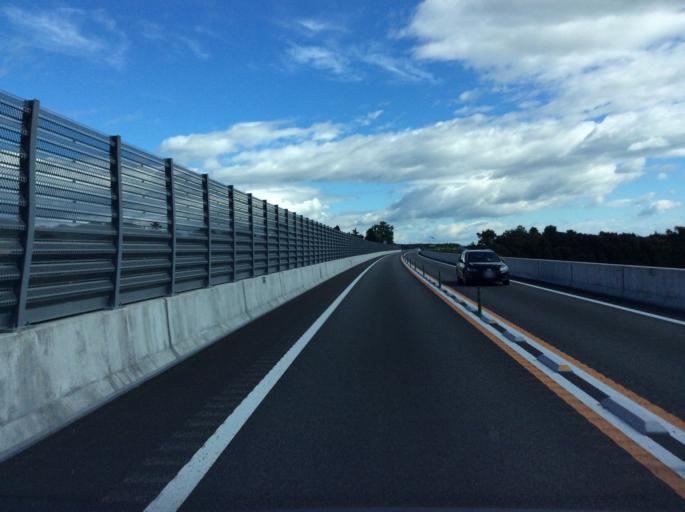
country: JP
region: Fukushima
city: Namie
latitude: 37.5975
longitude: 140.9262
